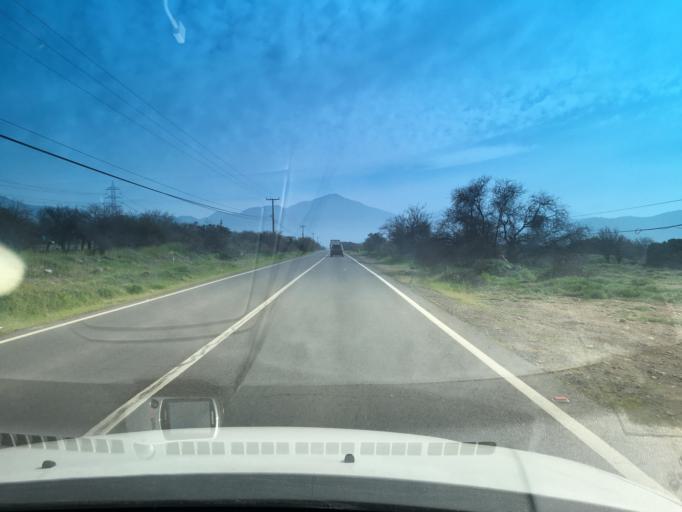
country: CL
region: Santiago Metropolitan
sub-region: Provincia de Chacabuco
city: Lampa
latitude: -33.1352
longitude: -70.9190
